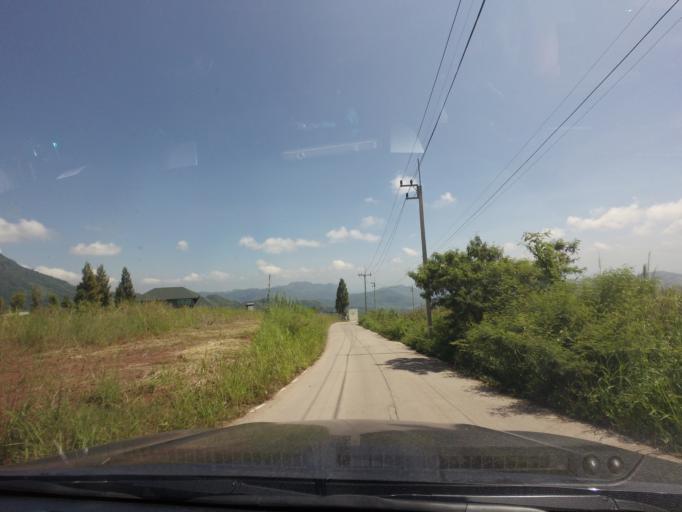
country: TH
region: Phetchabun
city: Khao Kho
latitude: 16.7940
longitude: 101.0425
